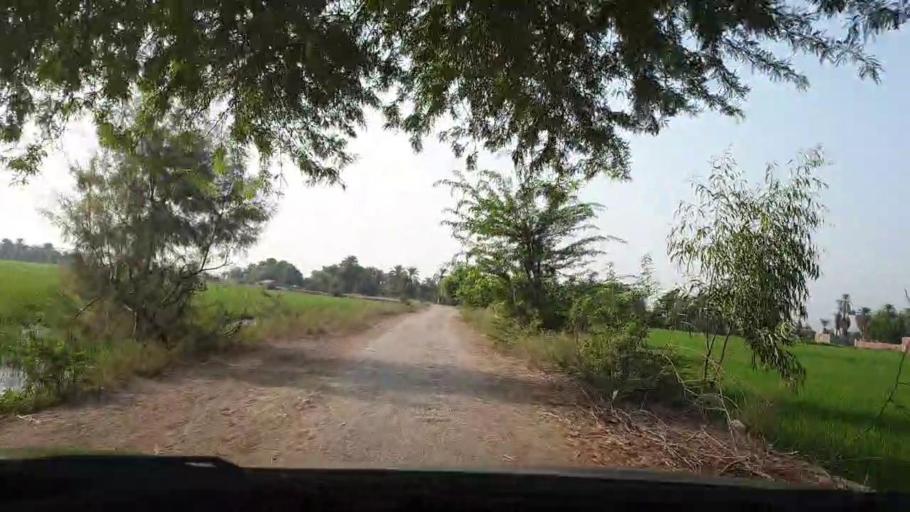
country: PK
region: Sindh
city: Larkana
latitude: 27.5135
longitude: 68.1782
